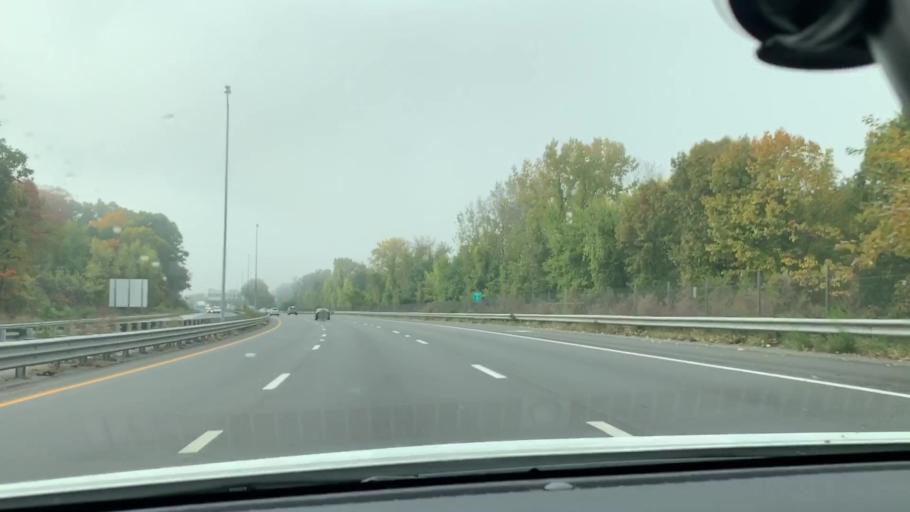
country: US
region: Massachusetts
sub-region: Hampden County
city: Longmeadow
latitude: 42.0714
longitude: -72.5876
